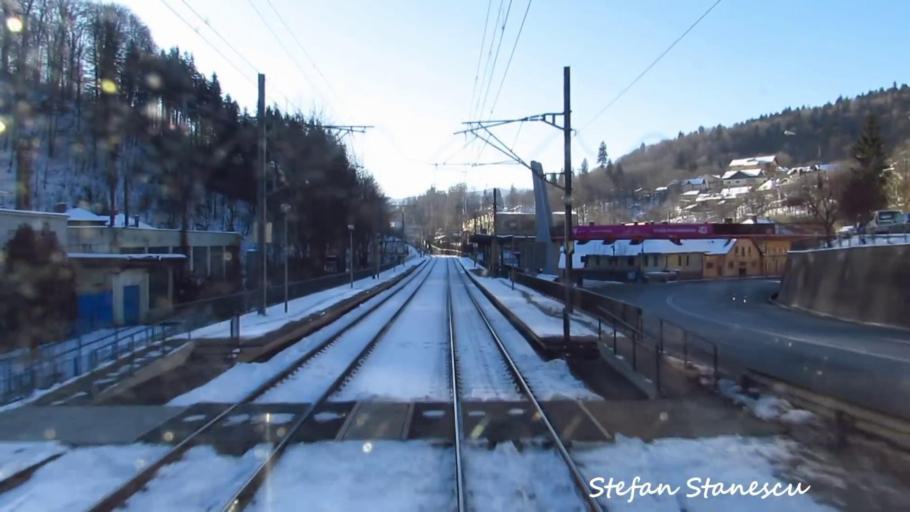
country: RO
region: Prahova
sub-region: Oras Sinaia
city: Sinaia
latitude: 45.3401
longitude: 25.5520
